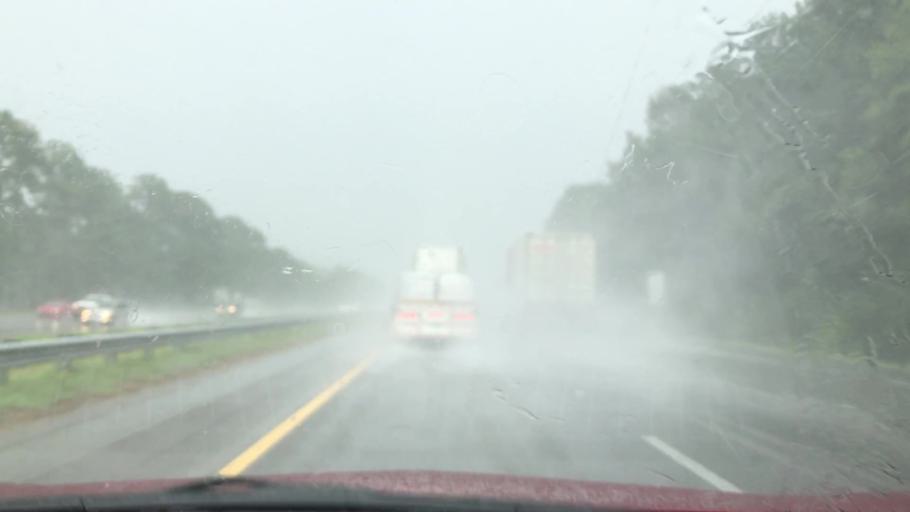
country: US
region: South Carolina
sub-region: Berkeley County
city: Ladson
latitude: 33.0038
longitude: -80.1005
